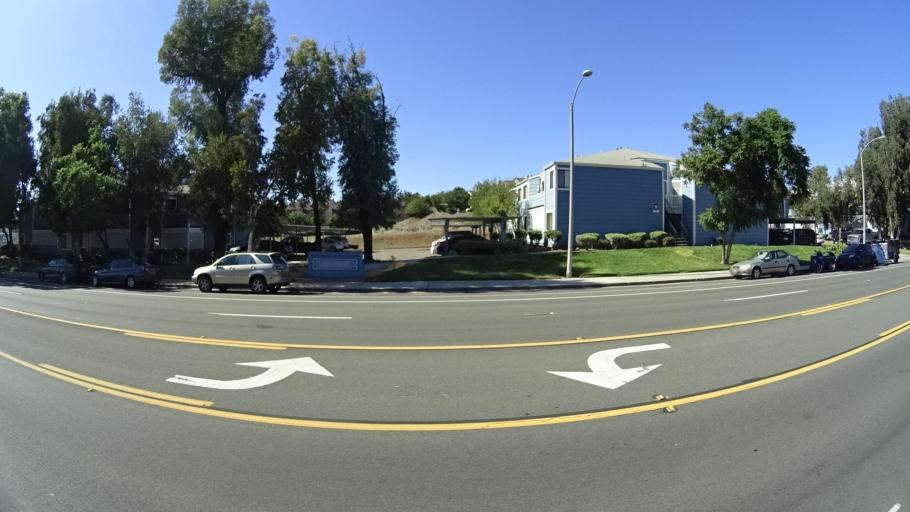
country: US
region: California
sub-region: San Diego County
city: Rancho San Diego
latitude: 32.7328
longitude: -116.9587
